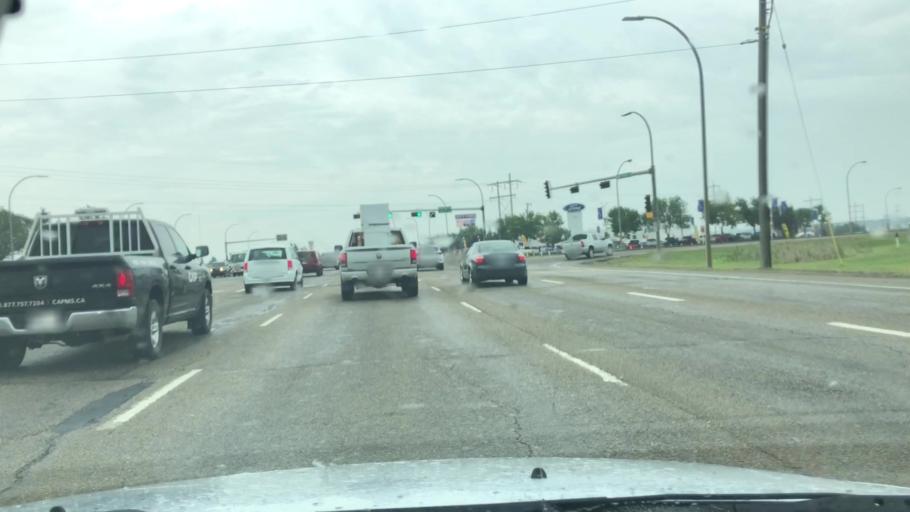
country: CA
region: Alberta
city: St. Albert
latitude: 53.6120
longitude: -113.5920
